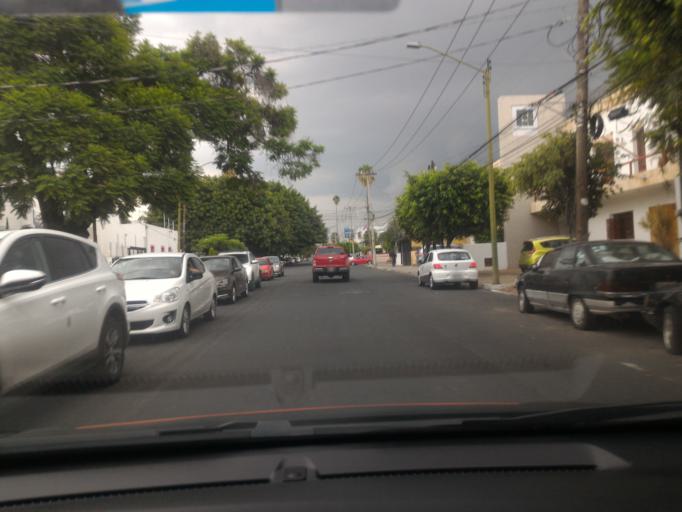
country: MX
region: Jalisco
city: Guadalajara
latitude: 20.6635
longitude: -103.3576
